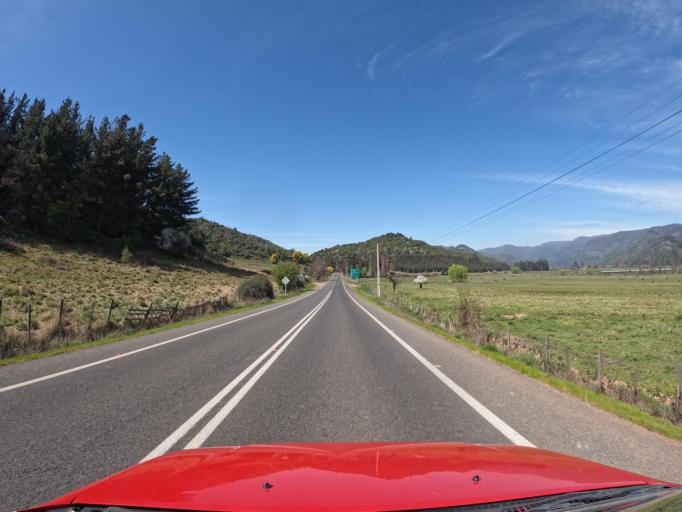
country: CL
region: Maule
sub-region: Provincia de Curico
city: Teno
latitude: -34.9780
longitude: -70.9739
